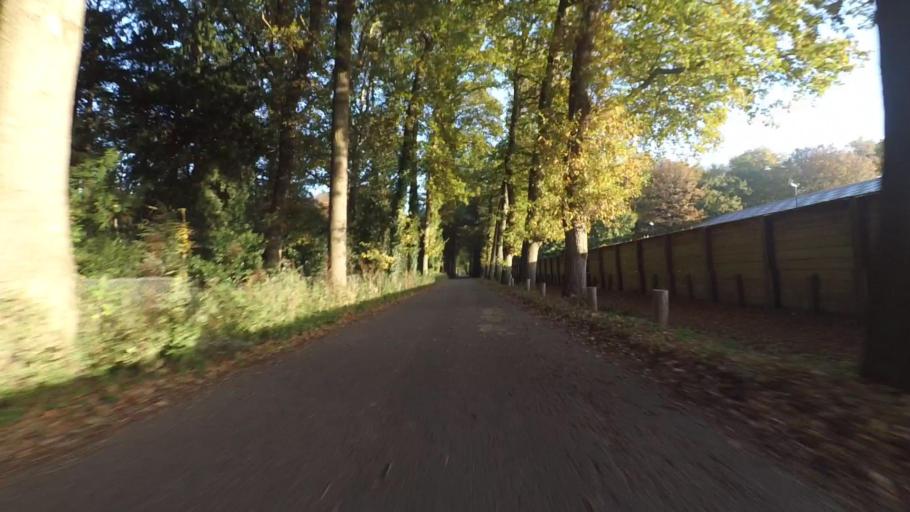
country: NL
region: Utrecht
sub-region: Gemeente De Bilt
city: De Bilt
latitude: 52.1620
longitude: 5.2009
